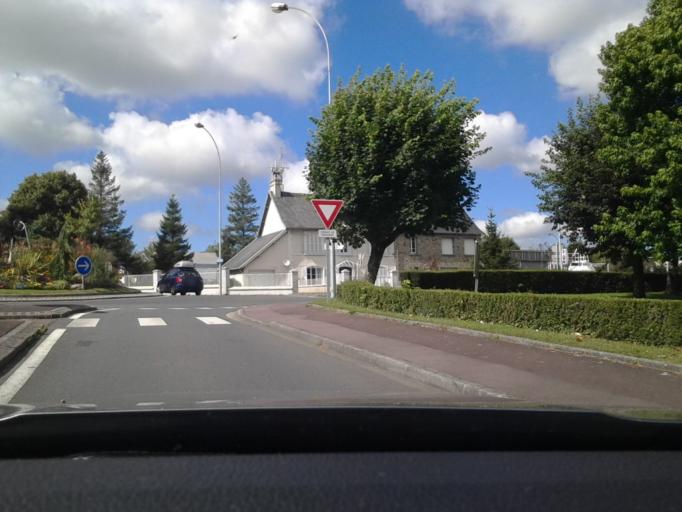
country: FR
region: Lower Normandy
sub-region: Departement de la Manche
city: Coutances
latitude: 49.0575
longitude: -1.4288
